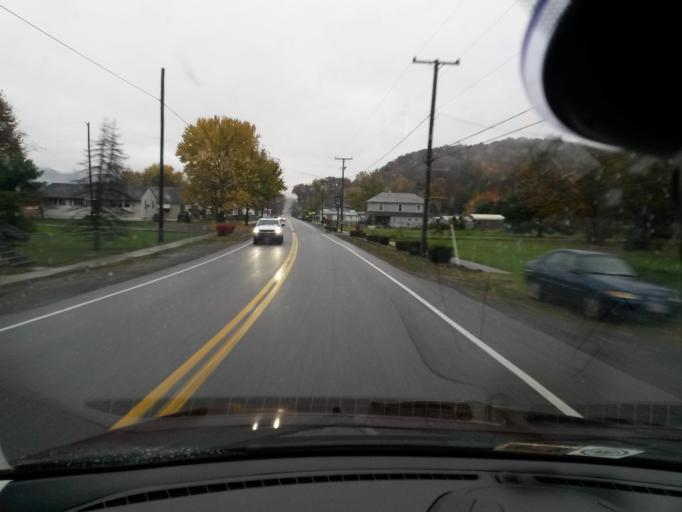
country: US
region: Virginia
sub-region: Alleghany County
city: Clifton Forge
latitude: 37.8003
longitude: -79.7936
